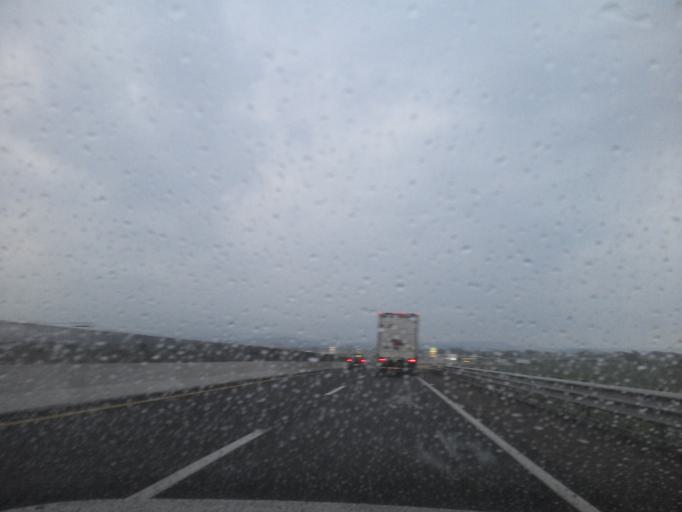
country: MX
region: Hidalgo
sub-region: Tula de Allende
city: Residencial Arboledas
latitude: 20.0962
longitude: -99.2950
